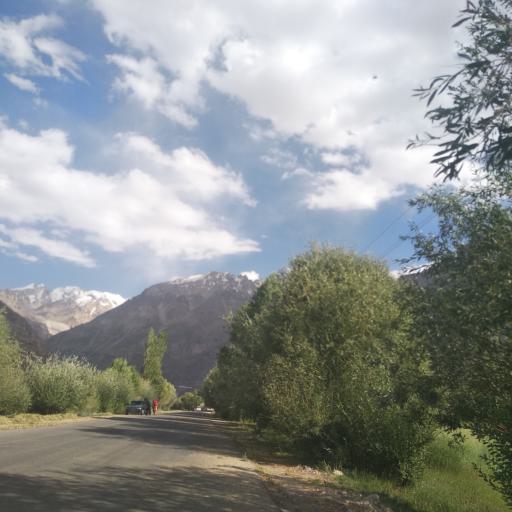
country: TJ
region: Gorno-Badakhshan
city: Roshtqal'a
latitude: 37.7257
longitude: 72.1606
